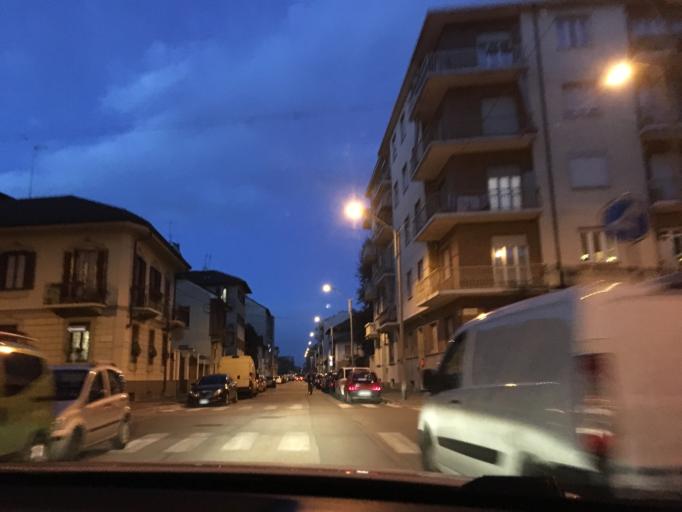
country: IT
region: Piedmont
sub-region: Provincia di Torino
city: Lesna
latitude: 45.0488
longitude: 7.6439
